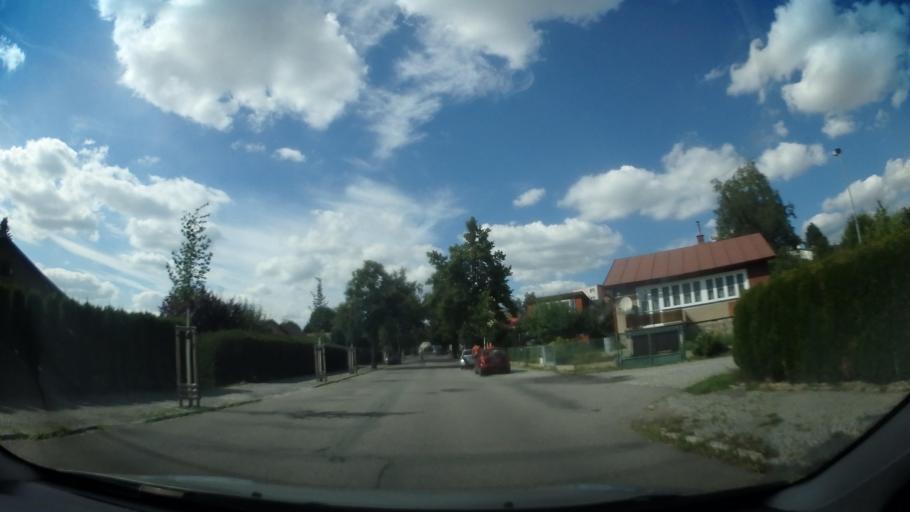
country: CZ
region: Vysocina
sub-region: Okres Zd'ar nad Sazavou
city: Zd'ar nad Sazavou
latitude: 49.5615
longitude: 15.9332
